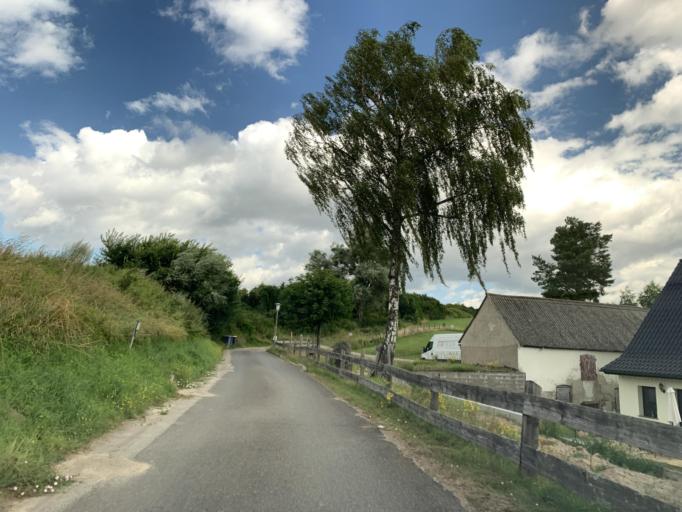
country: DE
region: Mecklenburg-Vorpommern
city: Carpin
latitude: 53.4070
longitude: 13.1995
